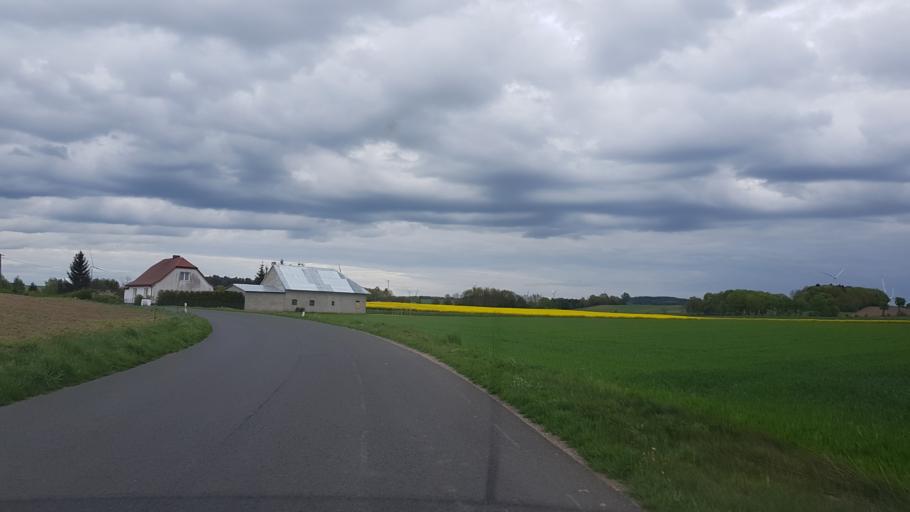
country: PL
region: West Pomeranian Voivodeship
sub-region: Powiat slawienski
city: Darlowo
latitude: 54.2733
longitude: 16.5061
